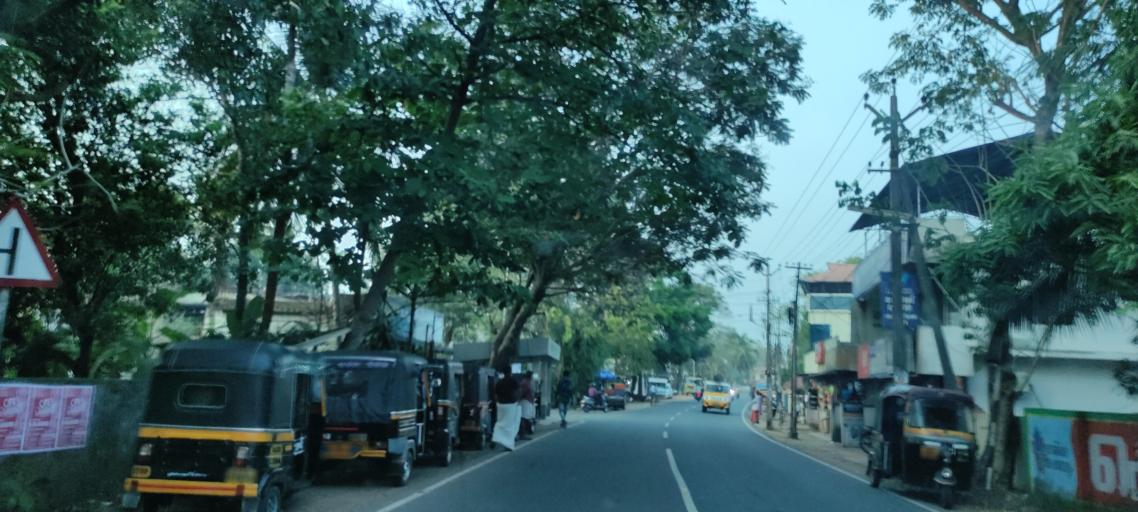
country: IN
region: Kerala
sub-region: Alappuzha
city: Mavelikara
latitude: 9.2797
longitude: 76.5308
